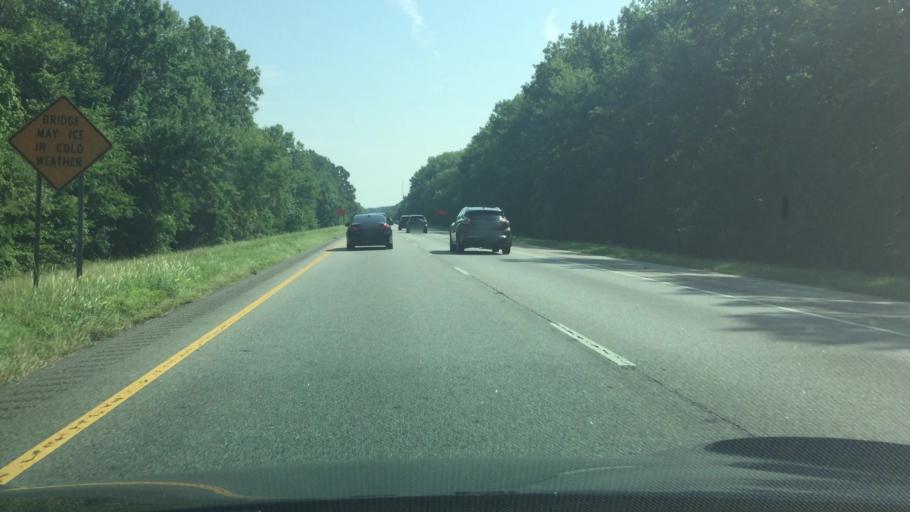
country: US
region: Alabama
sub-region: Montgomery County
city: Montgomery
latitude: 32.2201
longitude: -86.3966
